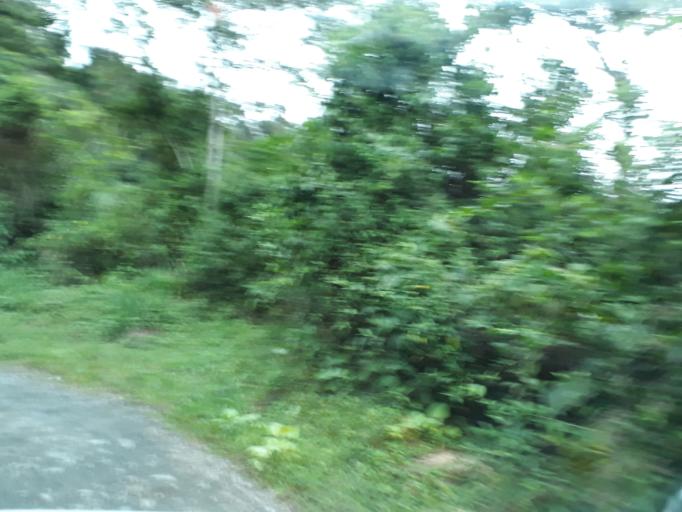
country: CO
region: Boyaca
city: Muzo
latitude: 5.3823
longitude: -74.0846
